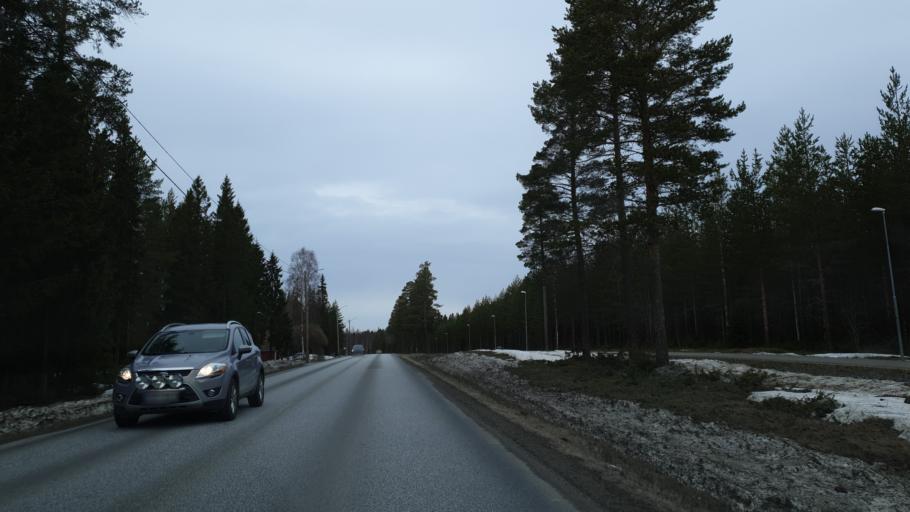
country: SE
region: Vaesterbotten
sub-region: Robertsfors Kommun
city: Robertsfors
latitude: 64.1728
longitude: 20.9119
